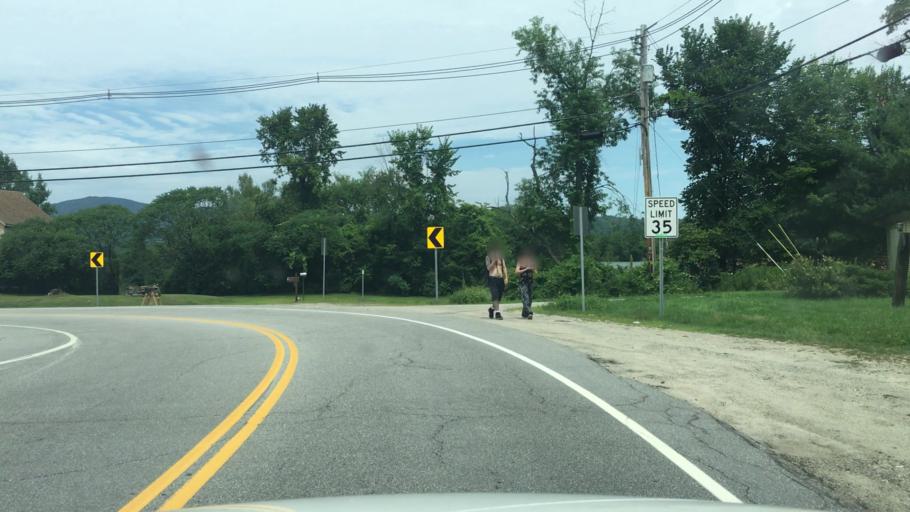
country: US
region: New Hampshire
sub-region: Grafton County
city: Plymouth
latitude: 43.7716
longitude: -71.7310
